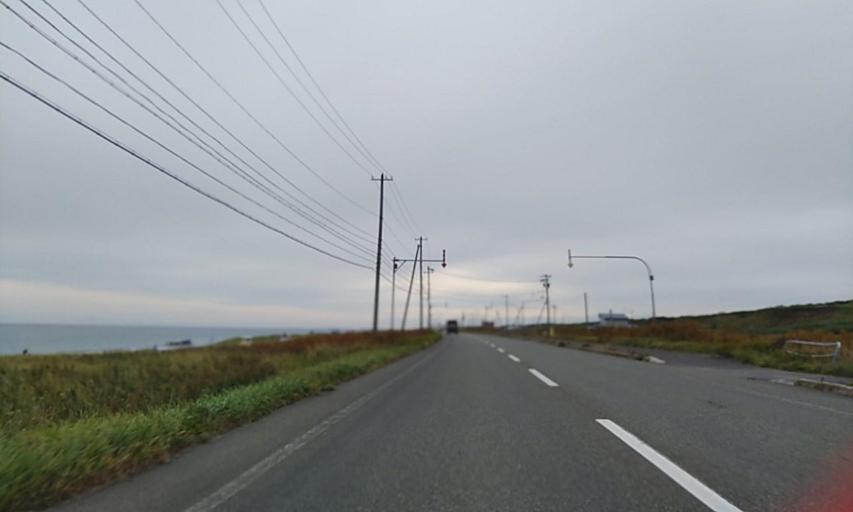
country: JP
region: Hokkaido
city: Makubetsu
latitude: 45.3615
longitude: 142.1248
